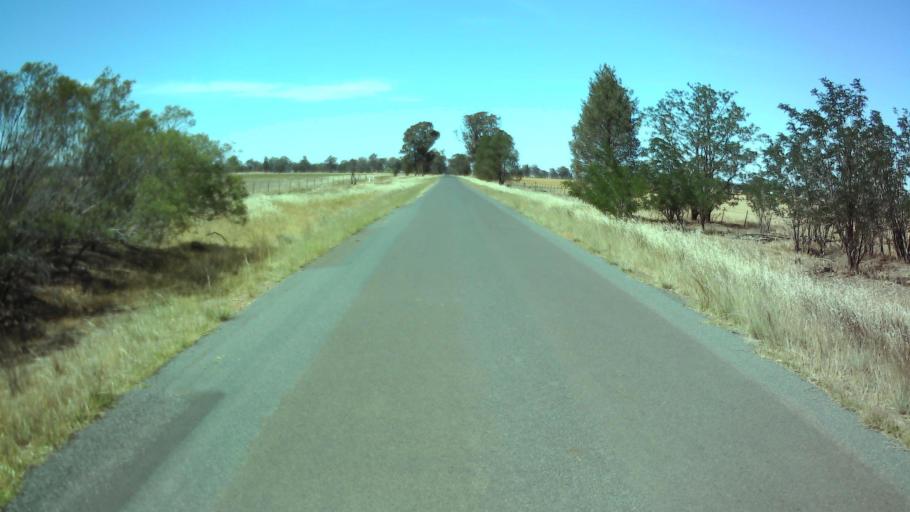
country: AU
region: New South Wales
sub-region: Weddin
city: Grenfell
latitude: -34.1034
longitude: 147.8872
